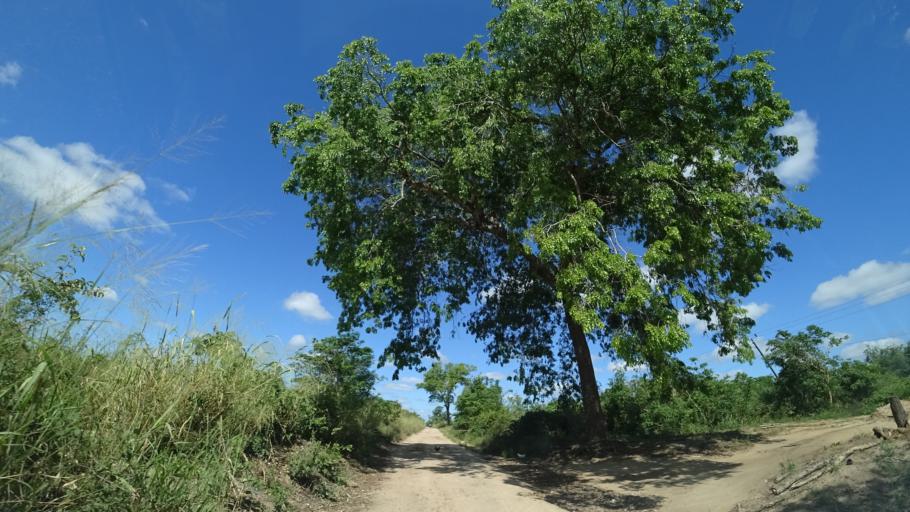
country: MZ
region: Sofala
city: Dondo
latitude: -19.3202
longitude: 34.6913
